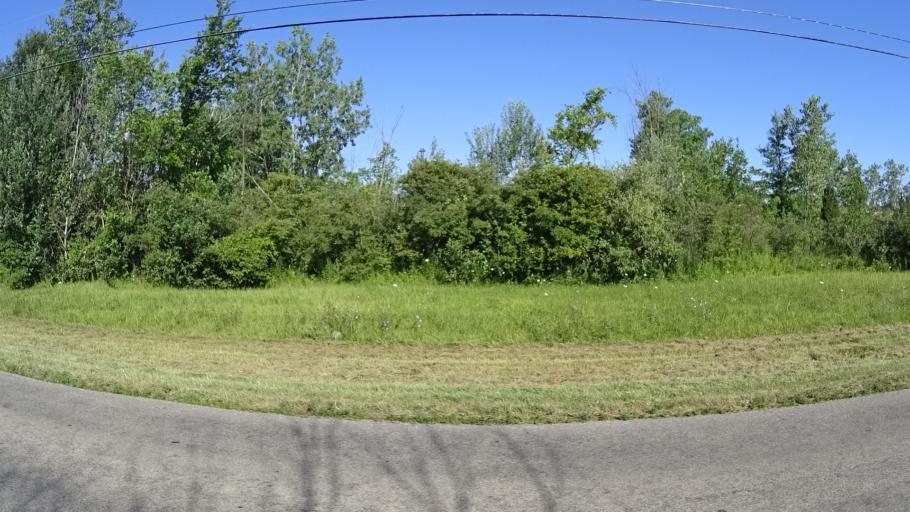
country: US
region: Ohio
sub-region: Erie County
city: Sandusky
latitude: 41.4196
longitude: -82.7371
